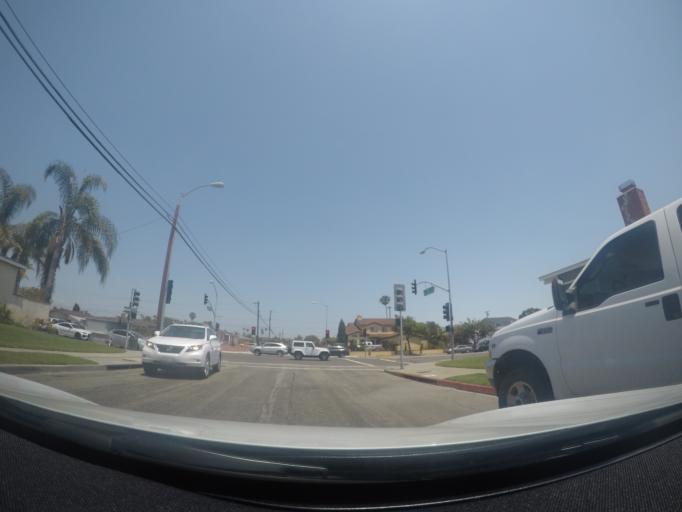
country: US
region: California
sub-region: Los Angeles County
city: Torrance
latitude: 33.8237
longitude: -118.3602
